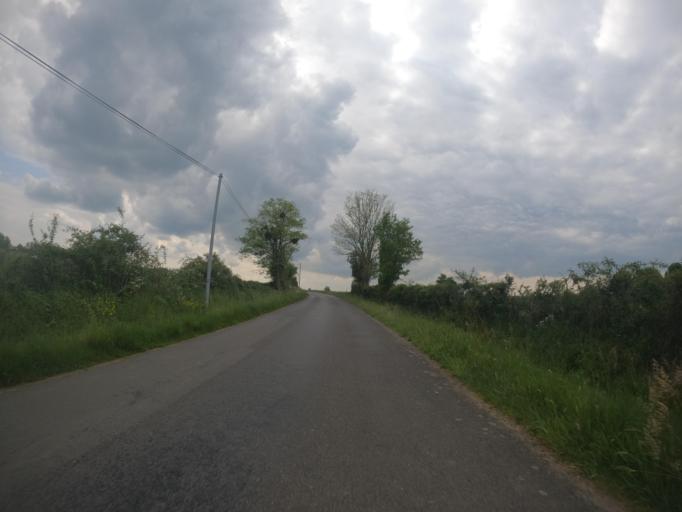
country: FR
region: Poitou-Charentes
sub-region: Departement des Deux-Sevres
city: Saint-Varent
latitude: 46.8647
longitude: -0.3037
